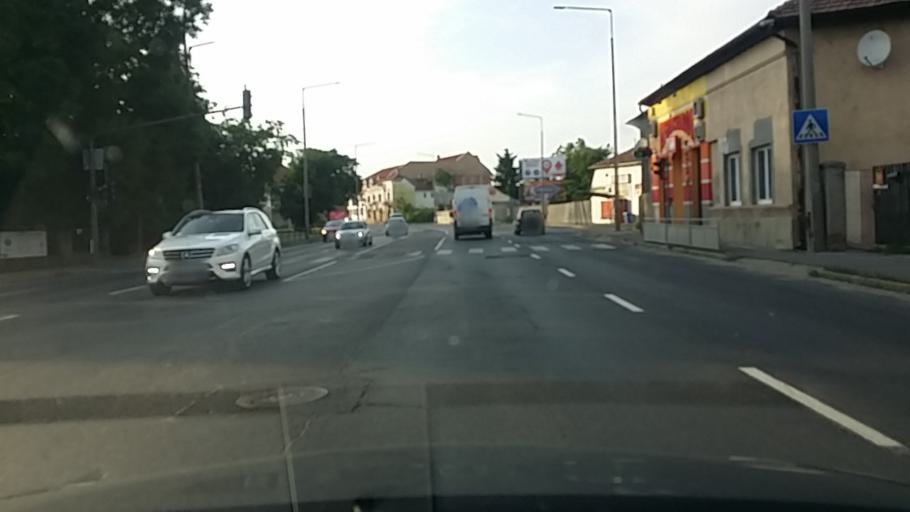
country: HU
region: Borsod-Abauj-Zemplen
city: Miskolc
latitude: 48.0719
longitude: 20.7895
